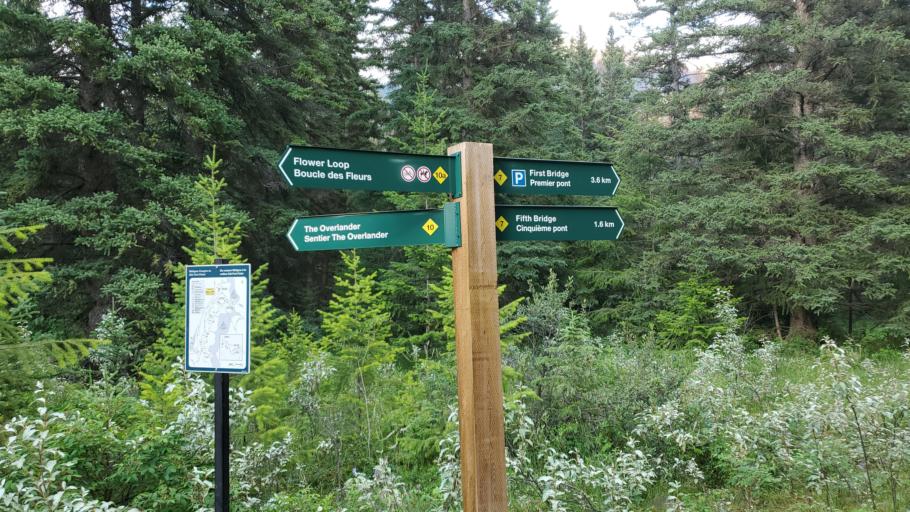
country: CA
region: Alberta
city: Jasper Park Lodge
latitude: 52.9337
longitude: -118.0296
